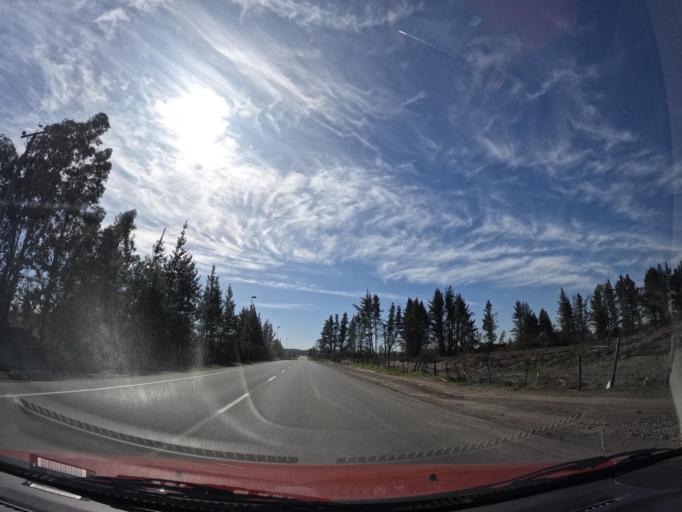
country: CL
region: Biobio
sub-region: Provincia de Biobio
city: Cabrero
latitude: -36.9392
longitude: -72.3456
